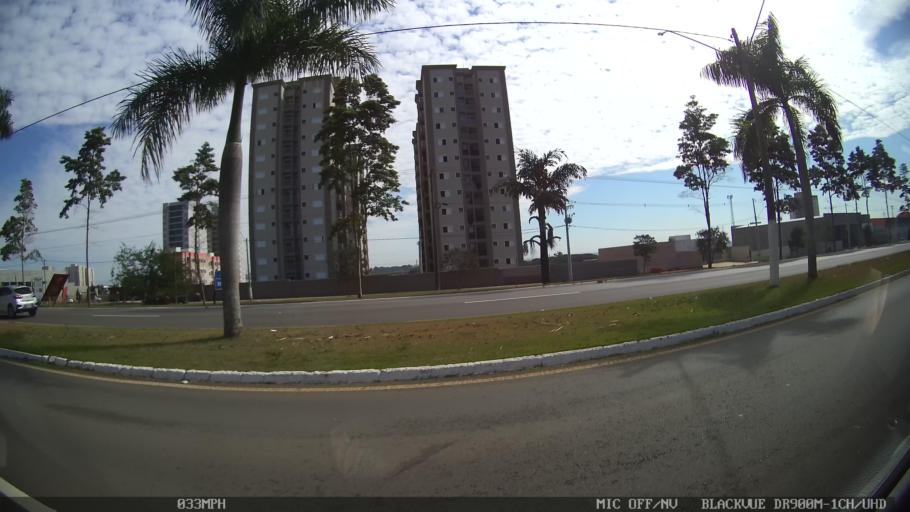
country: BR
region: Sao Paulo
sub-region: Santa Barbara D'Oeste
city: Santa Barbara d'Oeste
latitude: -22.7600
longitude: -47.4323
